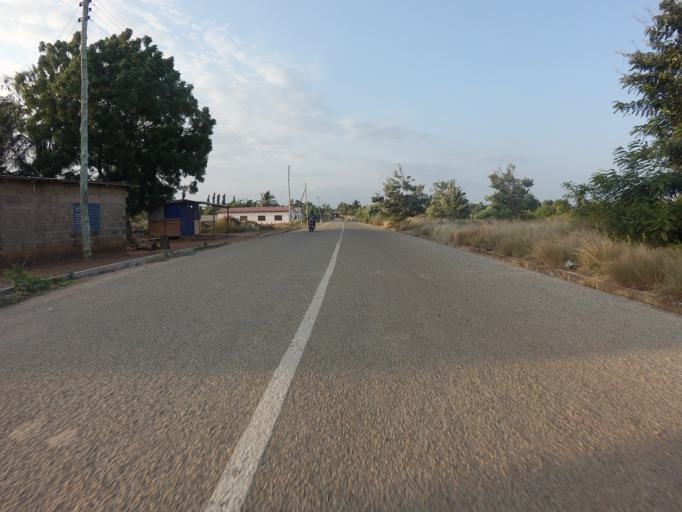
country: GH
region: Volta
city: Anloga
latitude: 6.0048
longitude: 0.5974
